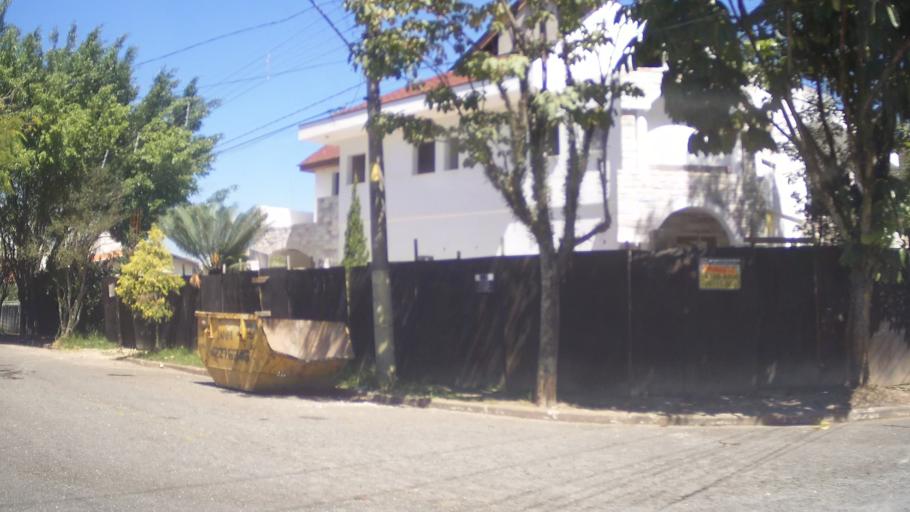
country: BR
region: Sao Paulo
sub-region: Sao Caetano Do Sul
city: Sao Caetano do Sul
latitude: -23.6389
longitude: -46.5775
